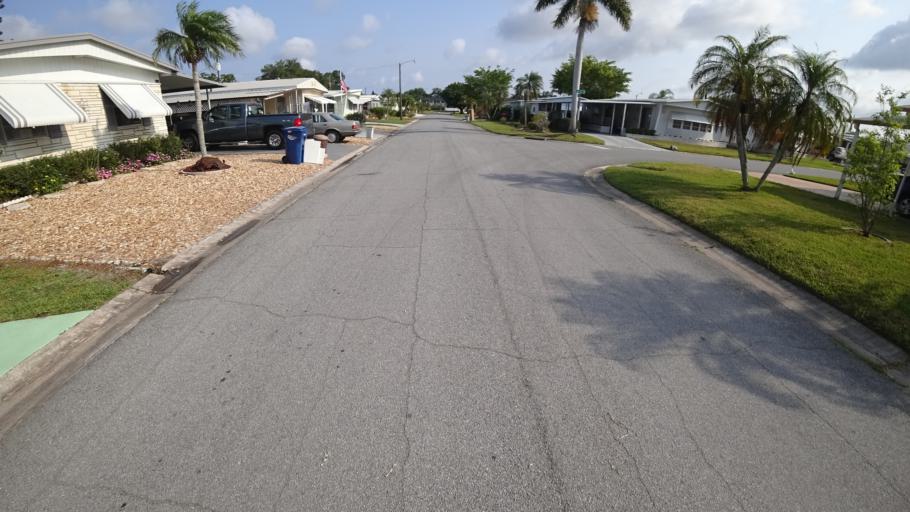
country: US
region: Florida
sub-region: Manatee County
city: West Samoset
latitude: 27.4554
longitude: -82.5656
